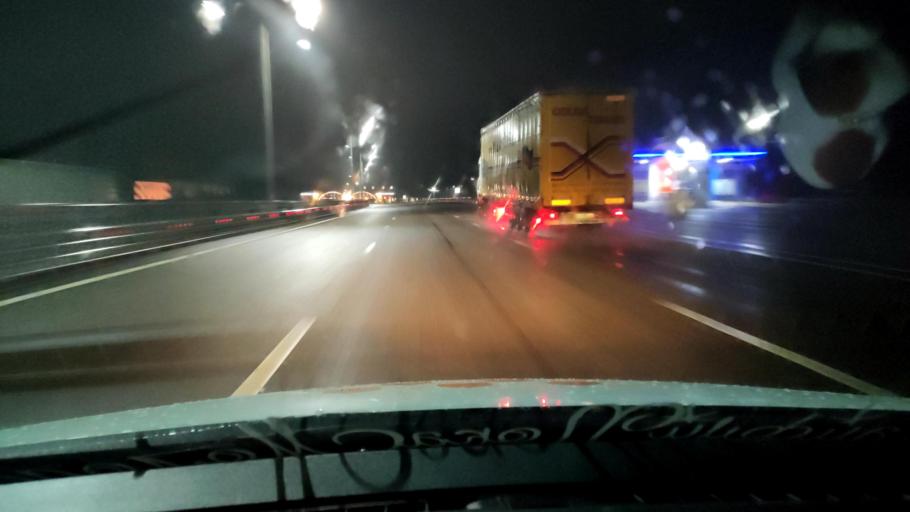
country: RU
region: Voronezj
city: Podgornoye
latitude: 51.8135
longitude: 39.2521
